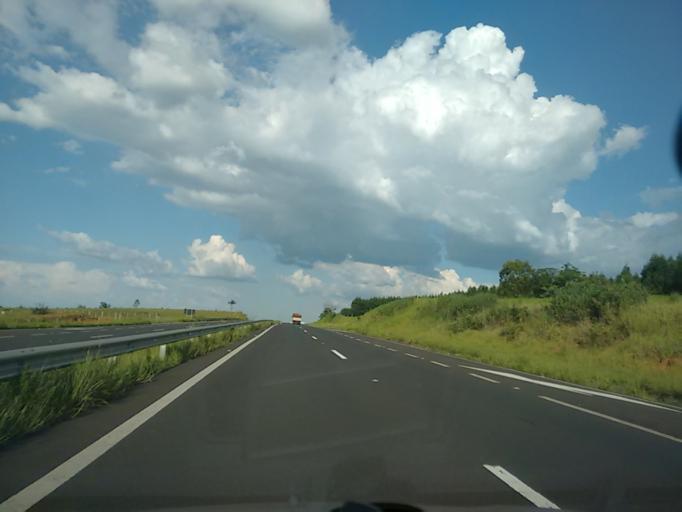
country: BR
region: Sao Paulo
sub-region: Duartina
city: Duartina
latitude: -22.3261
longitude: -49.4310
